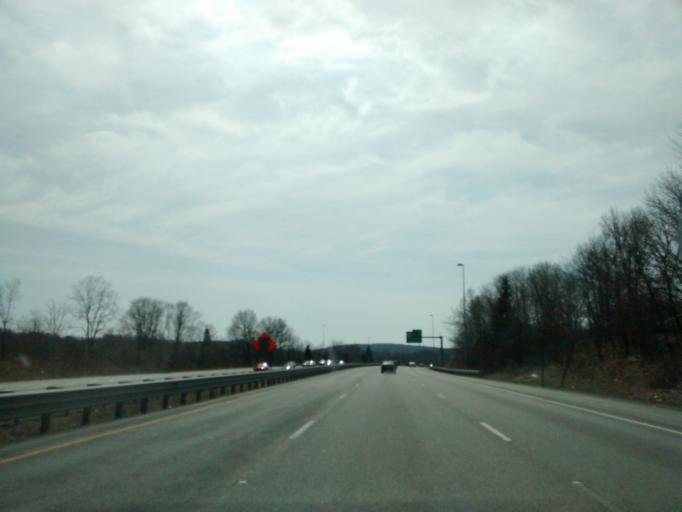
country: US
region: Massachusetts
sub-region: Worcester County
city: Auburn
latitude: 42.2044
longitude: -71.8401
